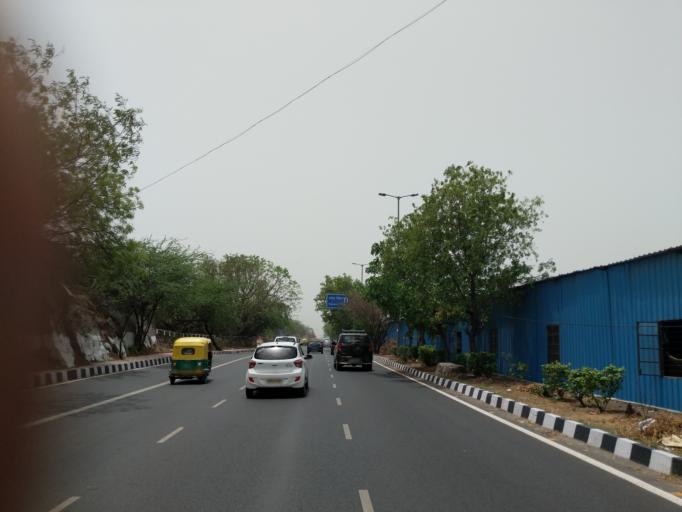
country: IN
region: NCT
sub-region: Central Delhi
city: Karol Bagh
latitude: 28.5463
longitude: 77.1611
